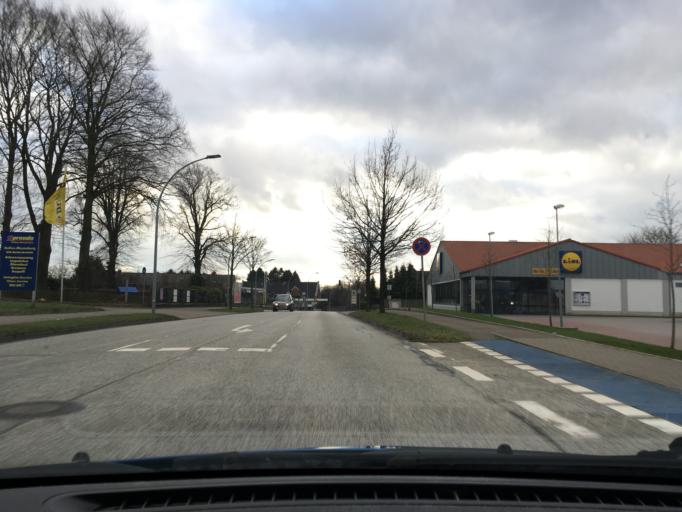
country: DE
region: Schleswig-Holstein
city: Ottenbuttel
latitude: 53.9515
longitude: 9.4944
